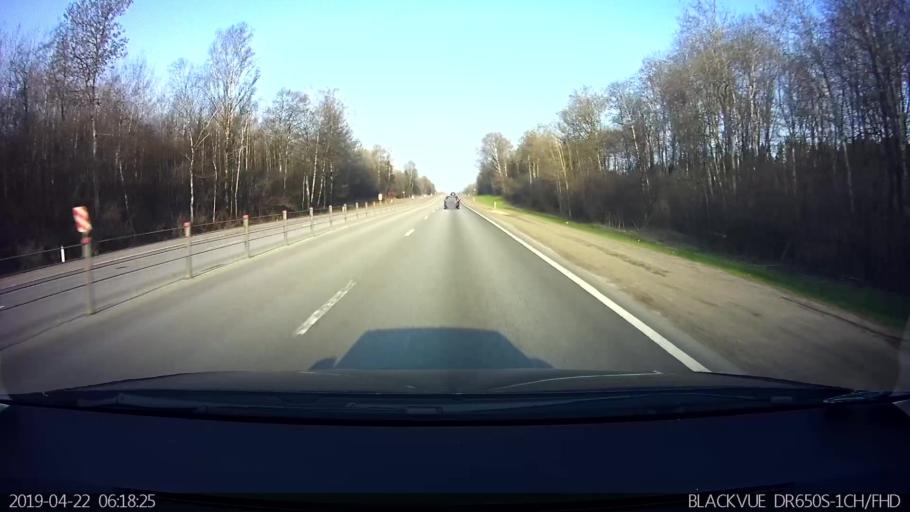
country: RU
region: Moskovskaya
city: Mozhaysk
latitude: 55.4632
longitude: 35.9600
